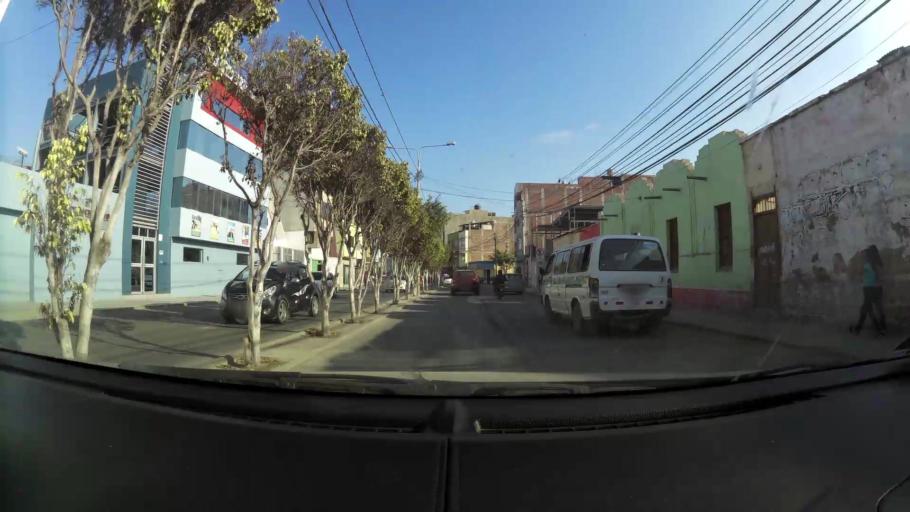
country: PE
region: Lambayeque
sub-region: Provincia de Chiclayo
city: Chiclayo
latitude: -6.7724
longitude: -79.8362
